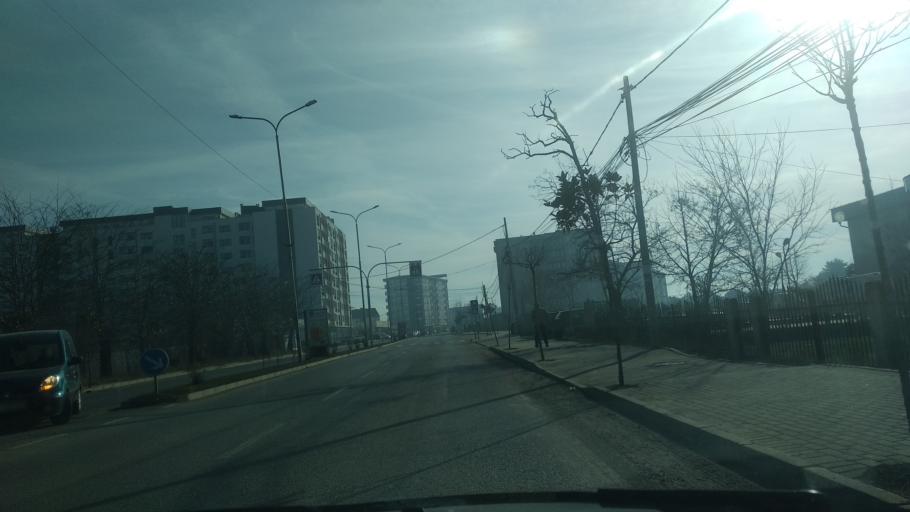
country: XK
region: Mitrovica
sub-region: Vushtrri
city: Vushtrri
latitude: 42.8193
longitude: 20.9779
